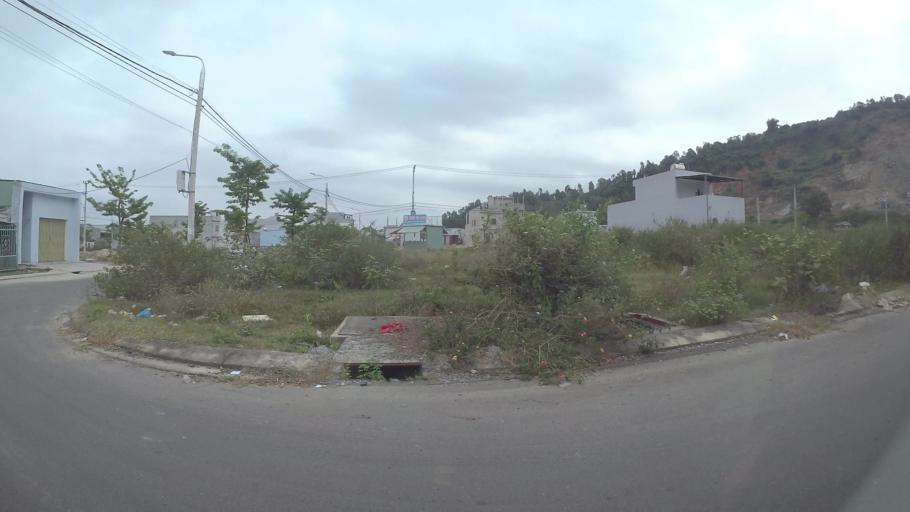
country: VN
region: Da Nang
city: Lien Chieu
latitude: 16.0419
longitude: 108.1681
